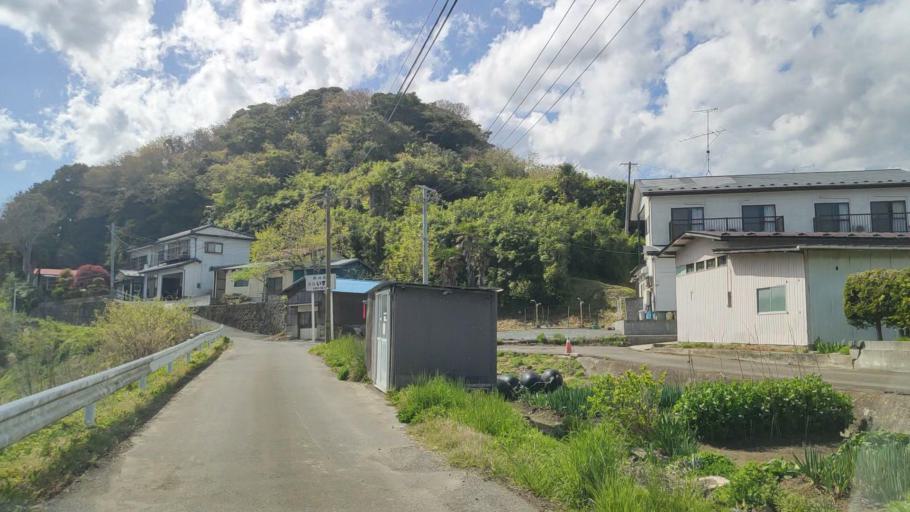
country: JP
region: Miyagi
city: Matsushima
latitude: 38.3368
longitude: 141.1433
